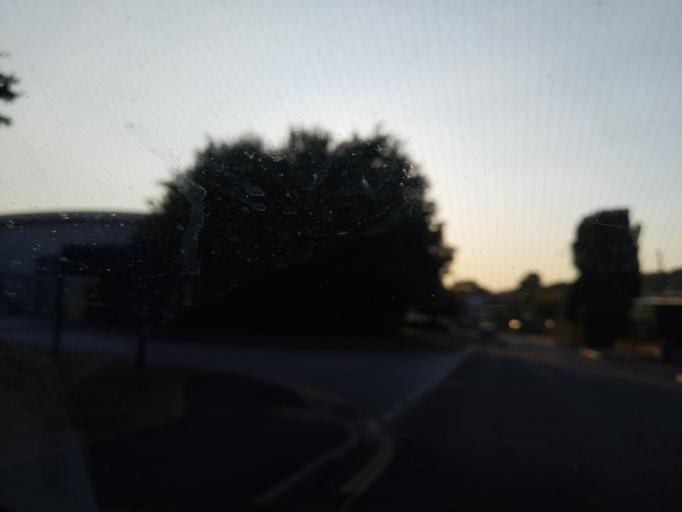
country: GB
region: England
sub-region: Devon
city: Plympton
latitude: 50.3941
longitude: -4.0872
